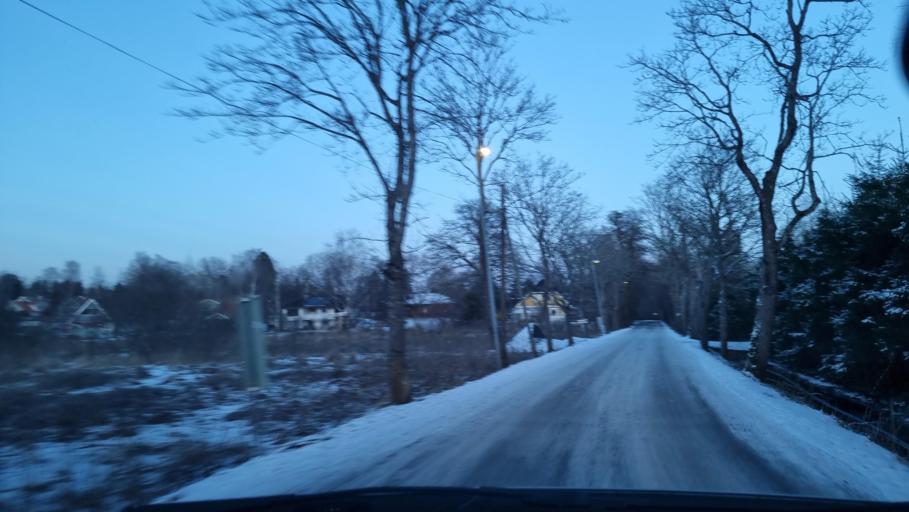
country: SE
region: Stockholm
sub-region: Vallentuna Kommun
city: Vallentuna
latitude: 59.5836
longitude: 18.1097
